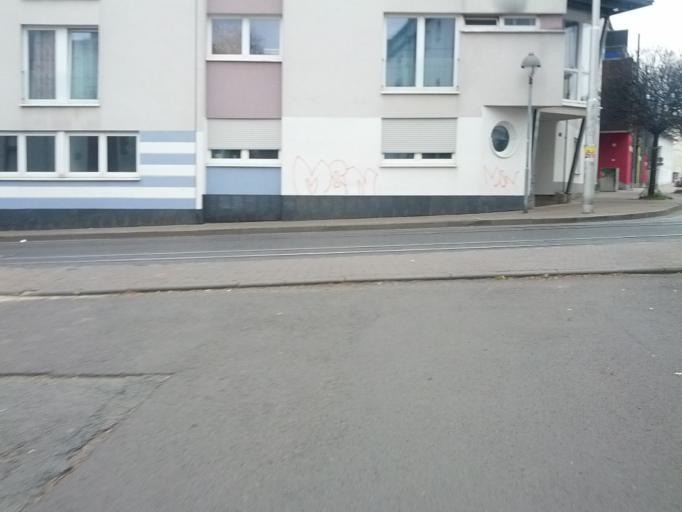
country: DE
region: Thuringia
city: Gotha
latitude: 50.9454
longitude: 10.6971
